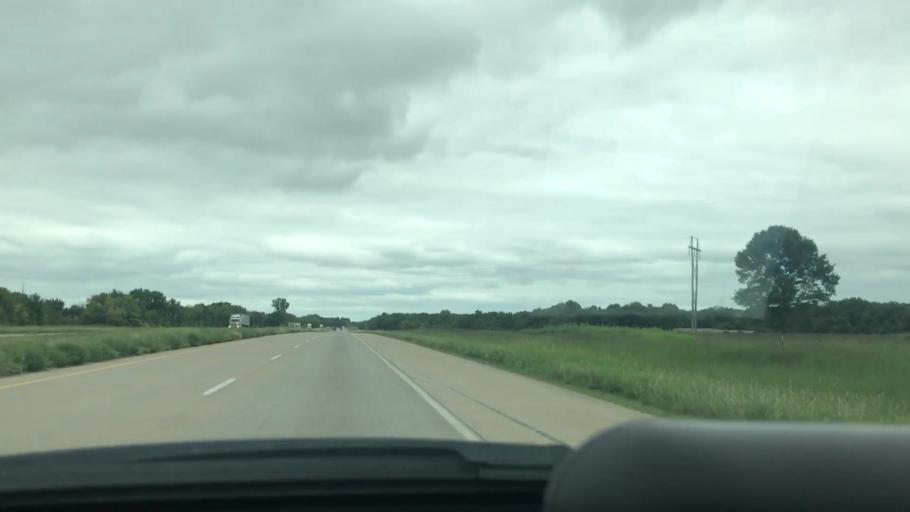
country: US
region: Oklahoma
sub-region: Mayes County
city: Chouteau
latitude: 36.2124
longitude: -95.3409
